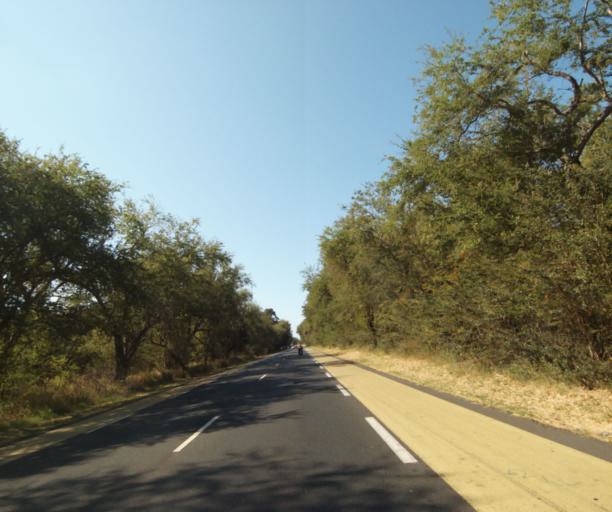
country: RE
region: Reunion
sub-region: Reunion
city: Saint-Paul
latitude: -21.0689
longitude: 55.2252
